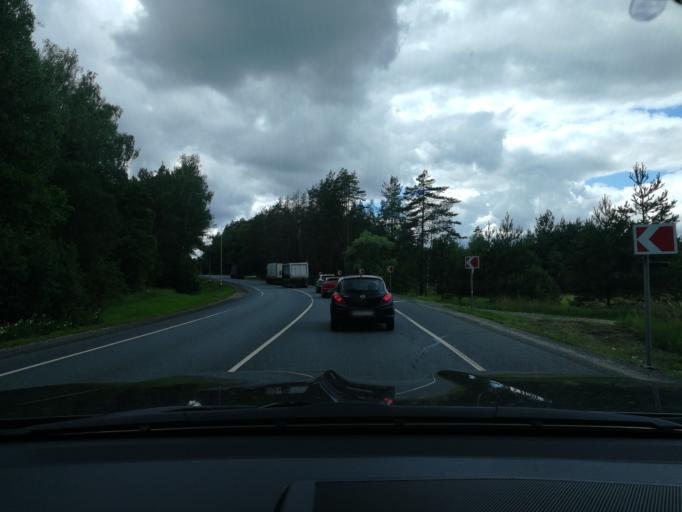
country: RU
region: Moskovskaya
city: Popovo
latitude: 55.0643
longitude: 37.7821
